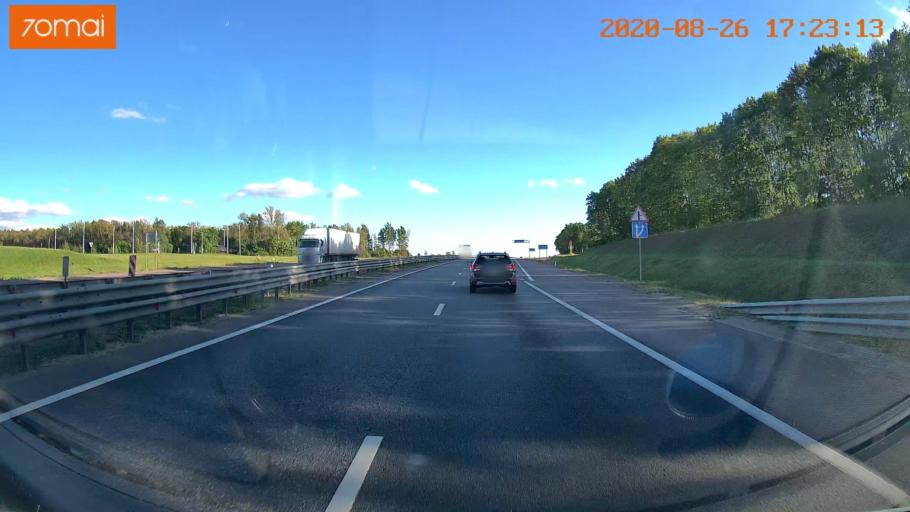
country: RU
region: Tula
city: Volovo
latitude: 53.5381
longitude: 38.1182
